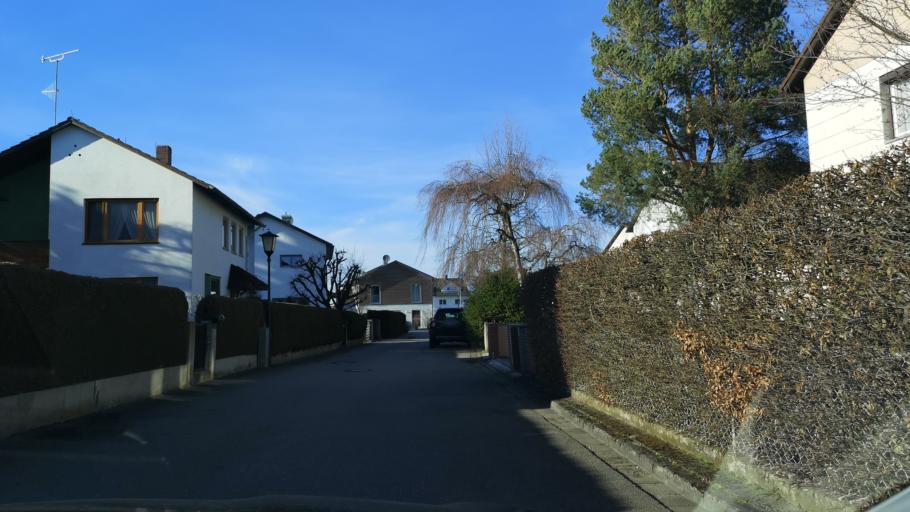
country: DE
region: Bavaria
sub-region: Upper Bavaria
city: Anzing
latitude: 48.1482
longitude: 11.8490
